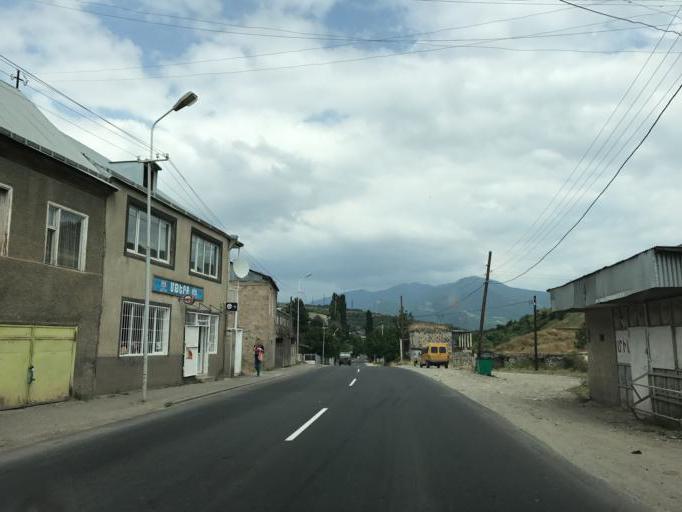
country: AM
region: Tavush
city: Haghartsin
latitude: 40.7750
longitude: 44.9740
